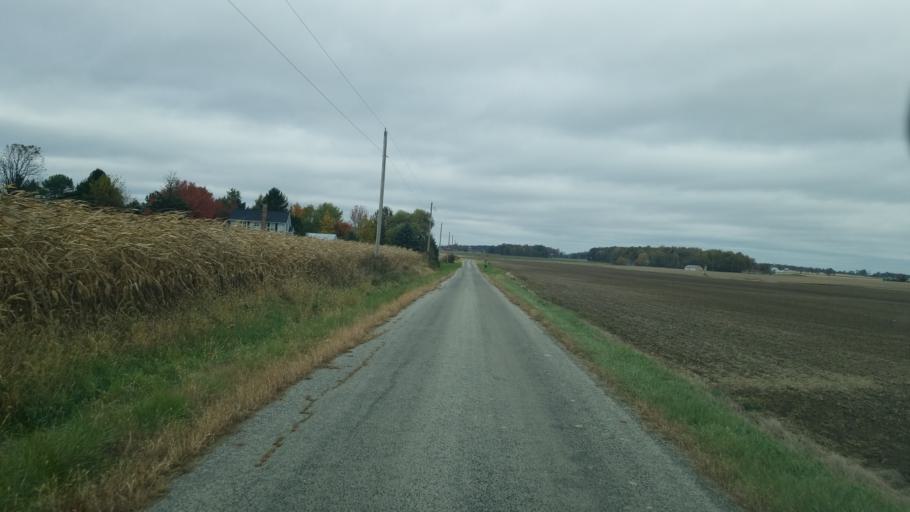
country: US
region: Ohio
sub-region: Huron County
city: Willard
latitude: 40.9249
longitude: -82.8442
